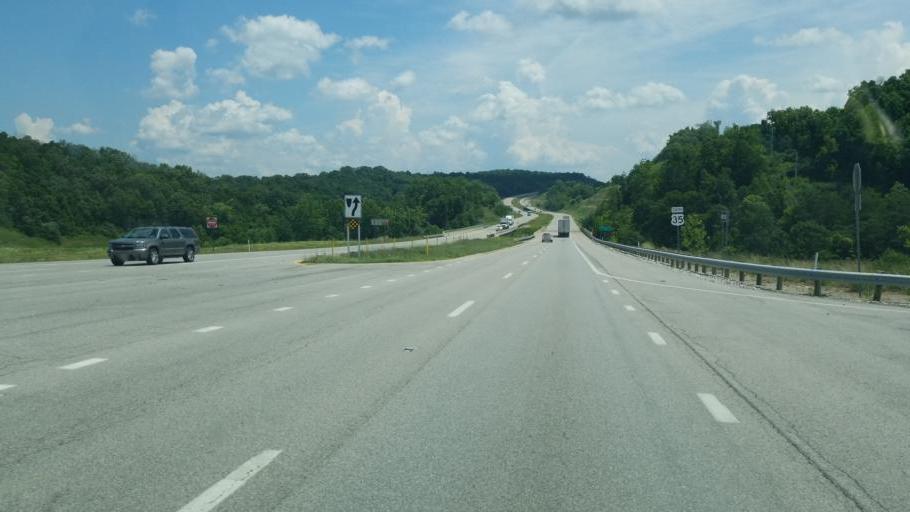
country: US
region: West Virginia
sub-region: Mason County
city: Point Pleasant
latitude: 38.7823
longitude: -82.0729
